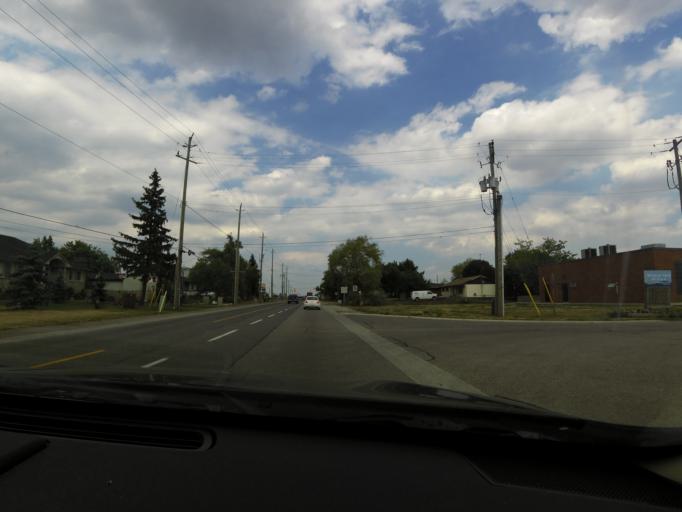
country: CA
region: Ontario
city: Brampton
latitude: 43.7719
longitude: -79.8799
